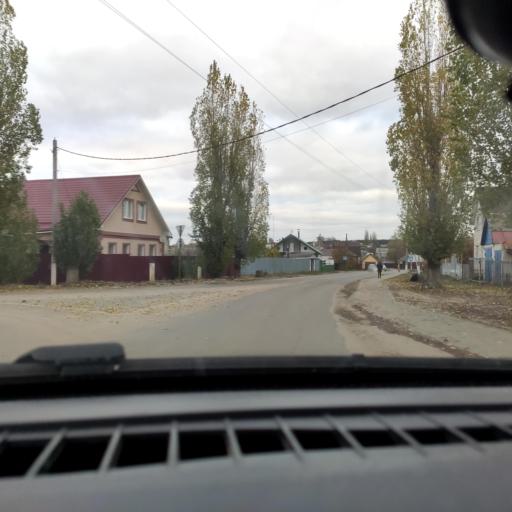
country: RU
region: Voronezj
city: Podgornoye
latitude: 51.7332
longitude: 39.1567
